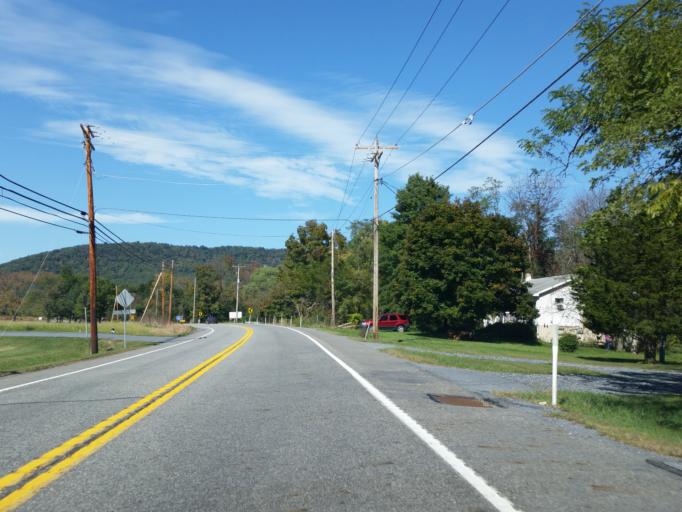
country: US
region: Pennsylvania
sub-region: Lebanon County
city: Jonestown
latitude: 40.4608
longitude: -76.5126
